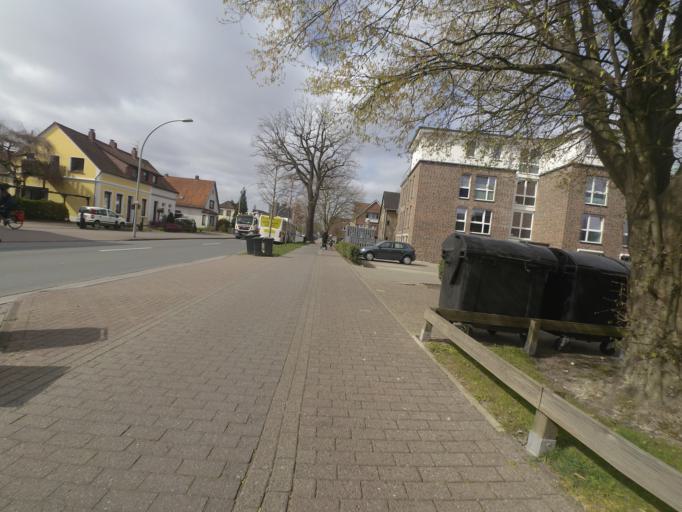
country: DE
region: Lower Saxony
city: Oldenburg
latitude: 53.1409
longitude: 8.1820
